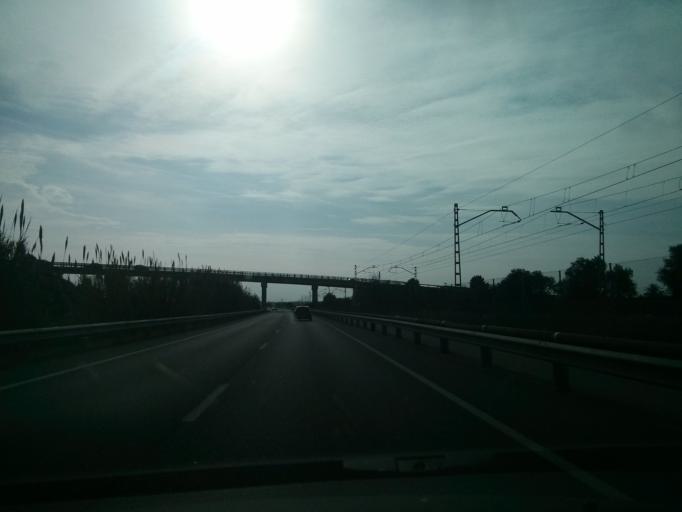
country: ES
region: Catalonia
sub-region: Provincia de Tarragona
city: El Vendrell
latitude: 41.2097
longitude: 1.5348
